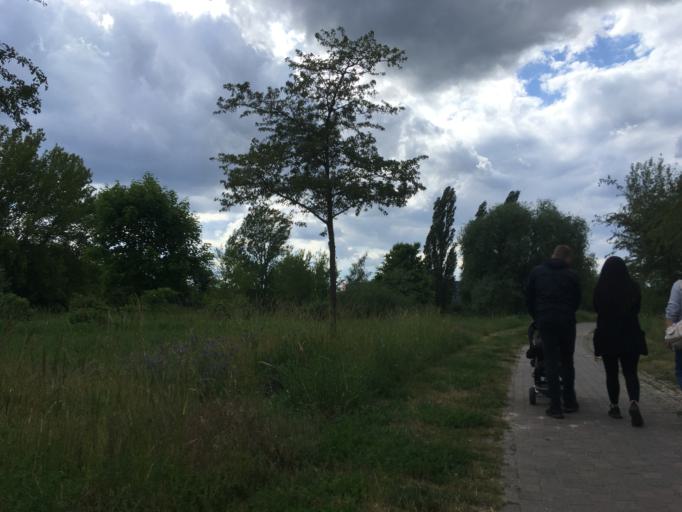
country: DE
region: Berlin
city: Falkenberg
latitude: 52.5672
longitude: 13.5420
